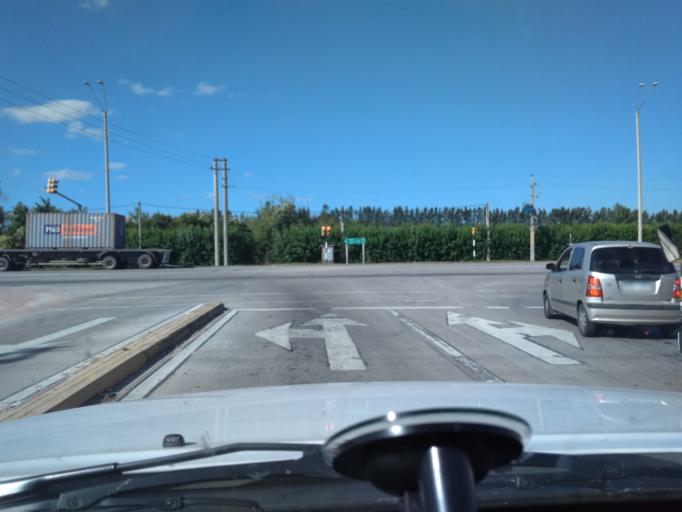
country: UY
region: Canelones
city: La Paz
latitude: -34.7915
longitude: -56.2111
